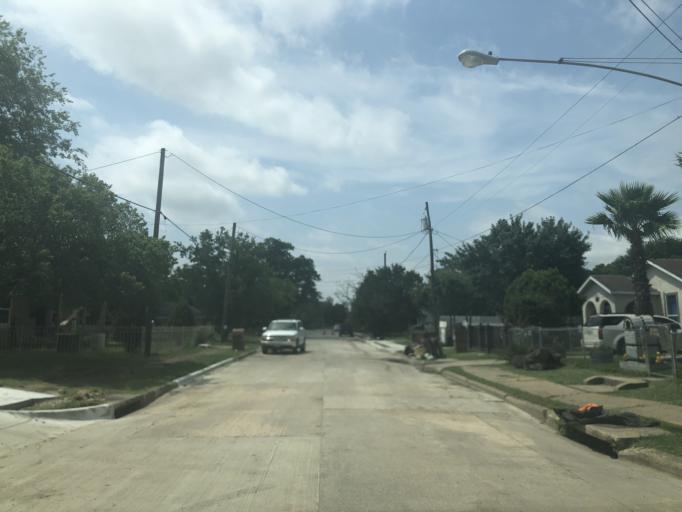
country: US
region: Texas
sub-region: Dallas County
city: Cockrell Hill
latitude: 32.7913
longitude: -96.8772
